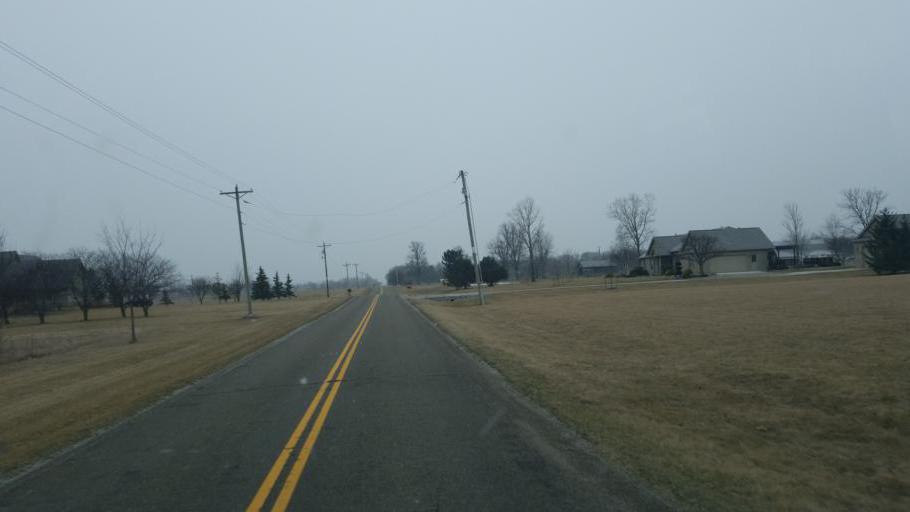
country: US
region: Ohio
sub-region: Defiance County
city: Hicksville
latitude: 41.3241
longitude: -84.7860
